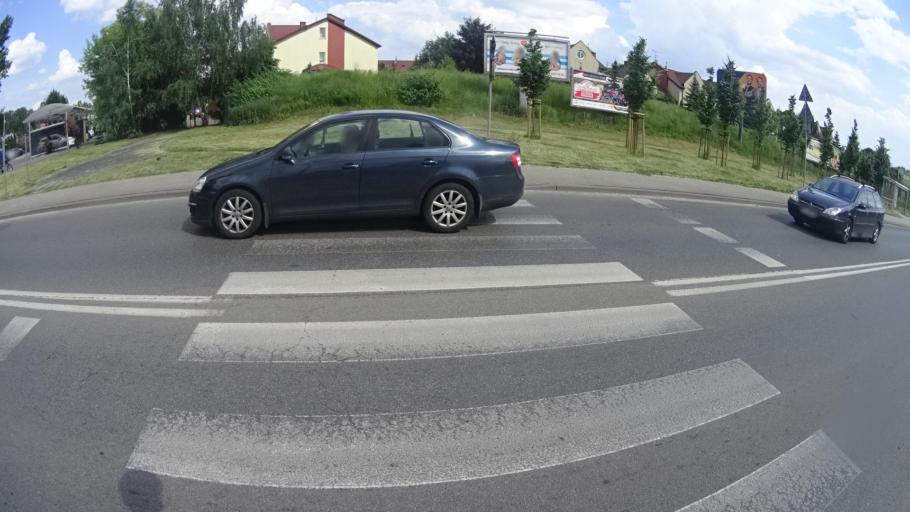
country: PL
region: Masovian Voivodeship
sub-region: Warszawa
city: Ursus
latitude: 52.2126
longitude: 20.9140
